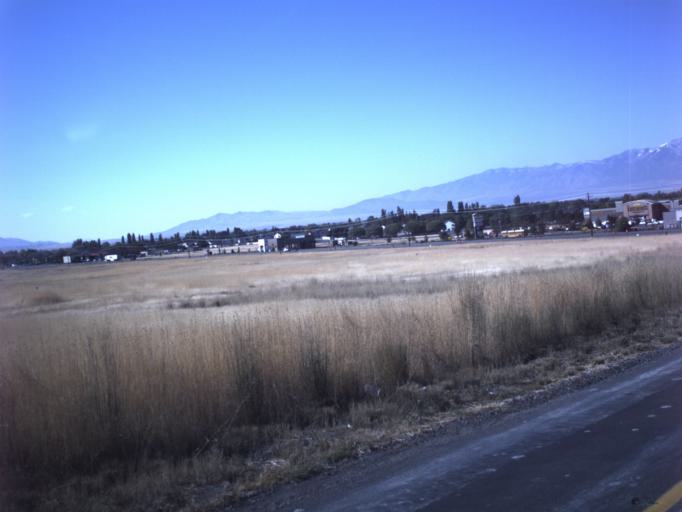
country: US
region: Utah
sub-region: Tooele County
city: Stansbury park
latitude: 40.6539
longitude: -112.2865
